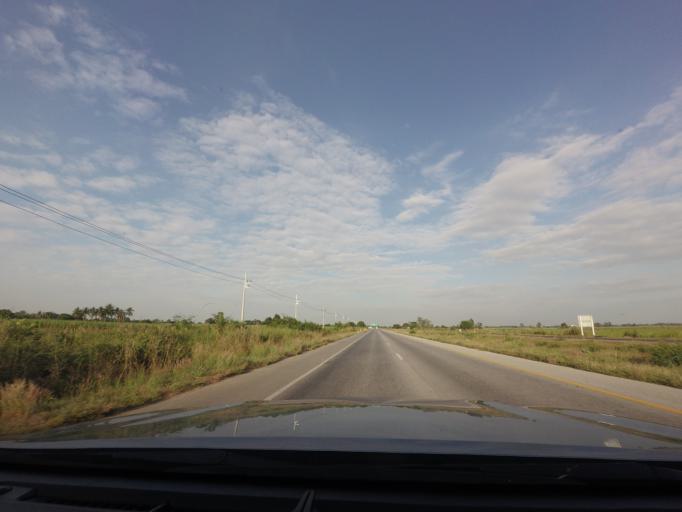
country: TH
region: Nakhon Sawan
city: Nakhon Sawan
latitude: 15.7614
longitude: 100.0972
